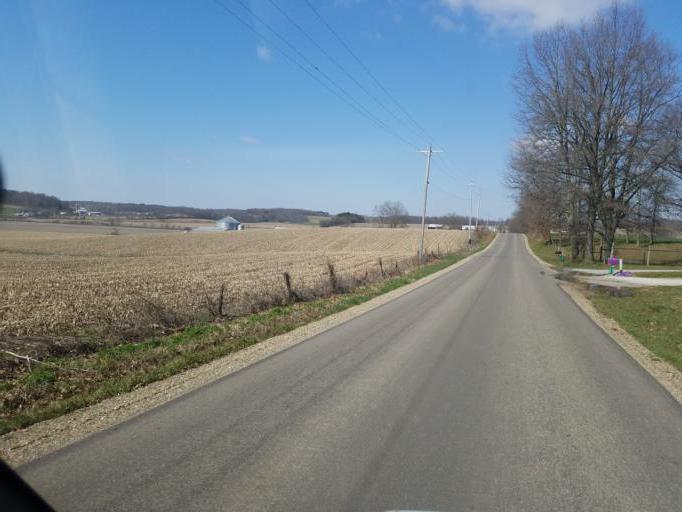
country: US
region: Ohio
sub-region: Licking County
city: Utica
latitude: 40.2479
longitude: -82.3528
